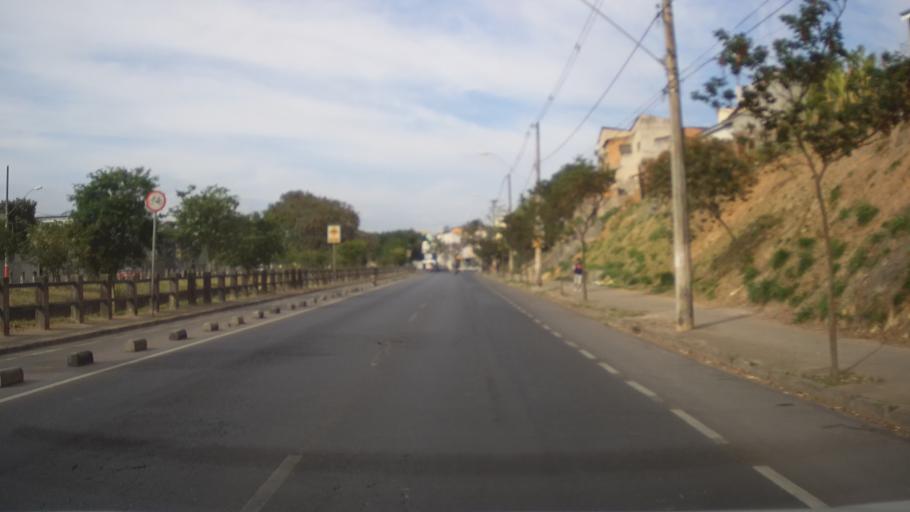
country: BR
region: Minas Gerais
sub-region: Contagem
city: Contagem
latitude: -19.8674
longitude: -44.0099
